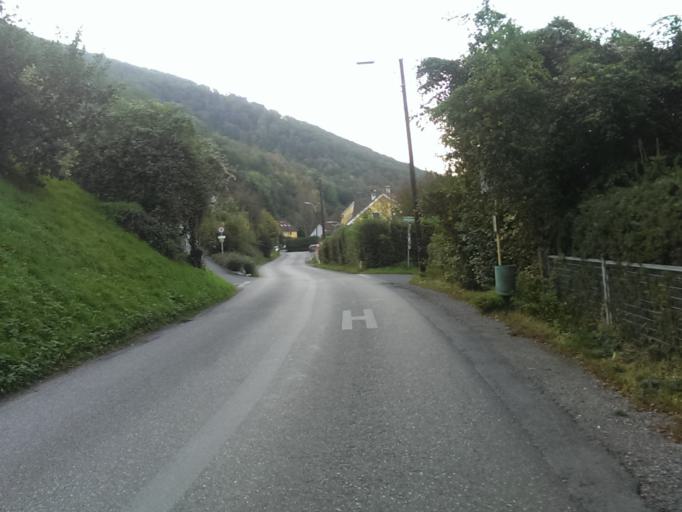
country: AT
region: Styria
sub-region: Graz Stadt
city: Goesting
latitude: 47.0888
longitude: 15.4008
